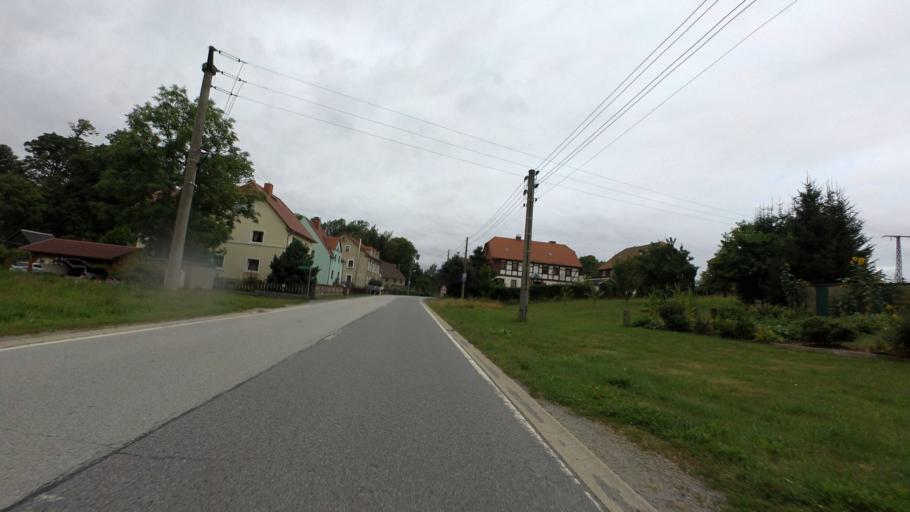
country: DE
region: Saxony
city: Berthelsdorf
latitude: 51.0682
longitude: 14.2072
